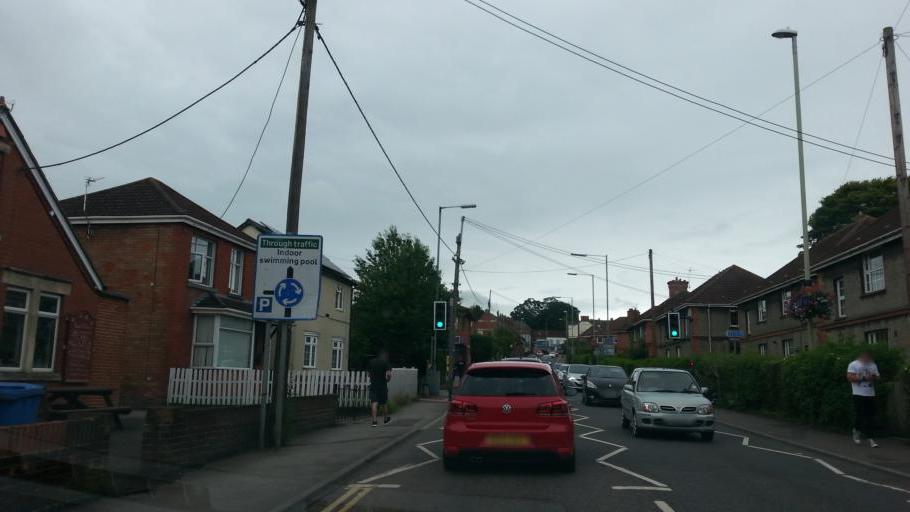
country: GB
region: England
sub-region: Wiltshire
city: Westbury
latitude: 51.2607
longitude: -2.1860
